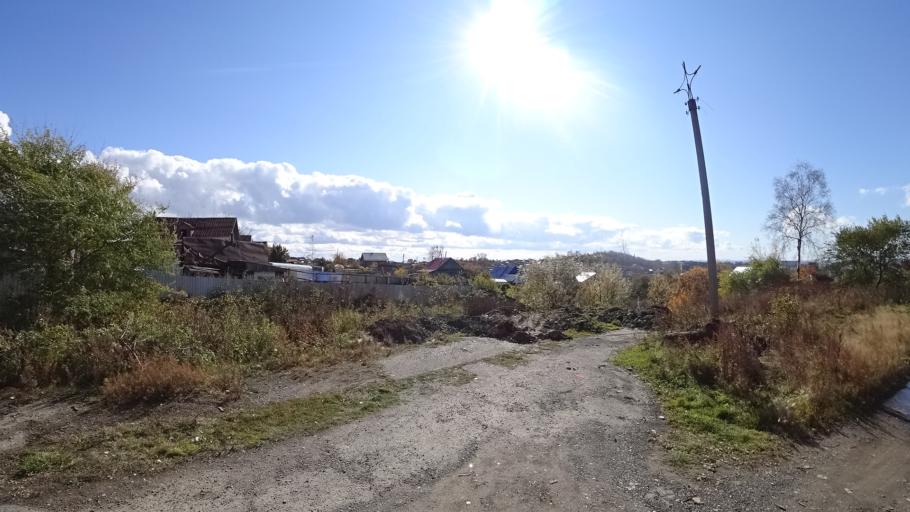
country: RU
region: Khabarovsk Krai
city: Amursk
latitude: 50.2380
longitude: 136.9172
